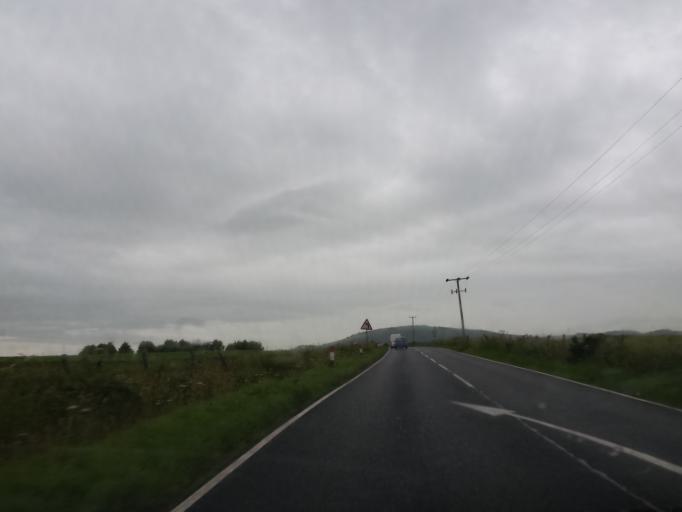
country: GB
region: Scotland
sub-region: Fife
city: Balmullo
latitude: 56.4078
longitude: -2.9137
